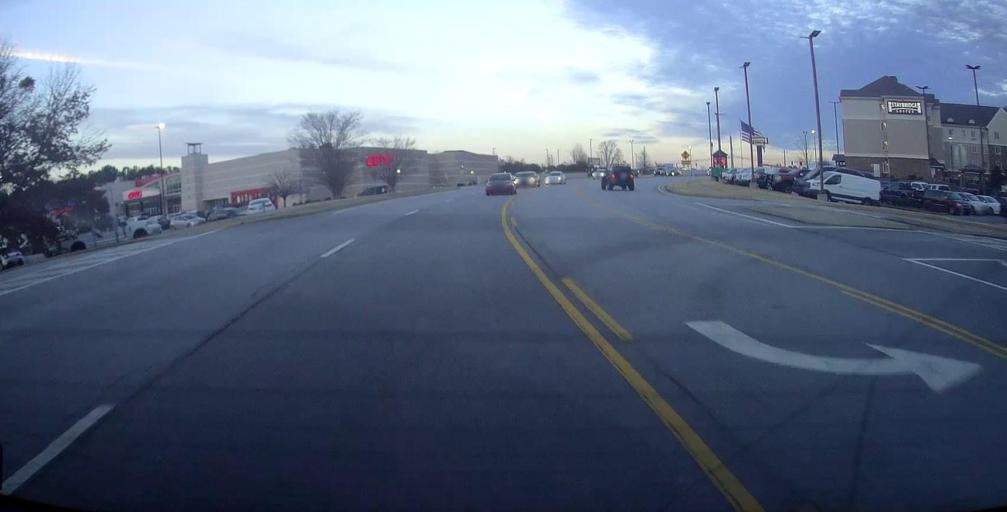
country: US
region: Alabama
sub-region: Russell County
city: Phenix City
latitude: 32.5386
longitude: -84.9689
